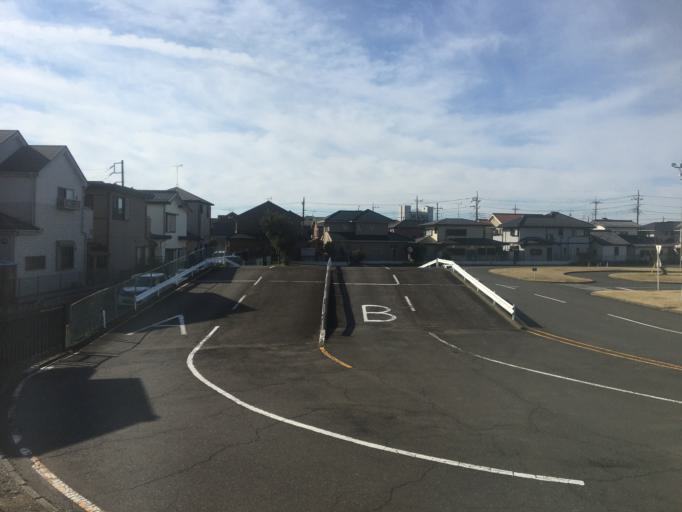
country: JP
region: Saitama
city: Kawagoe
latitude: 35.9245
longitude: 139.4484
